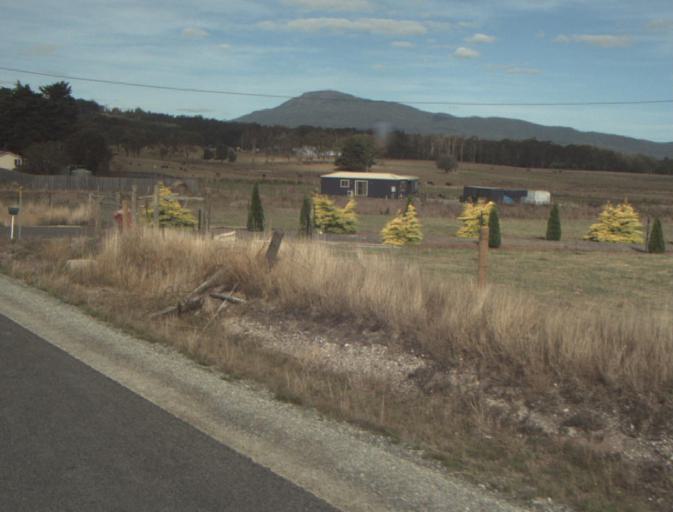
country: AU
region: Tasmania
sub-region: Launceston
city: Mayfield
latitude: -41.1987
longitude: 147.1817
